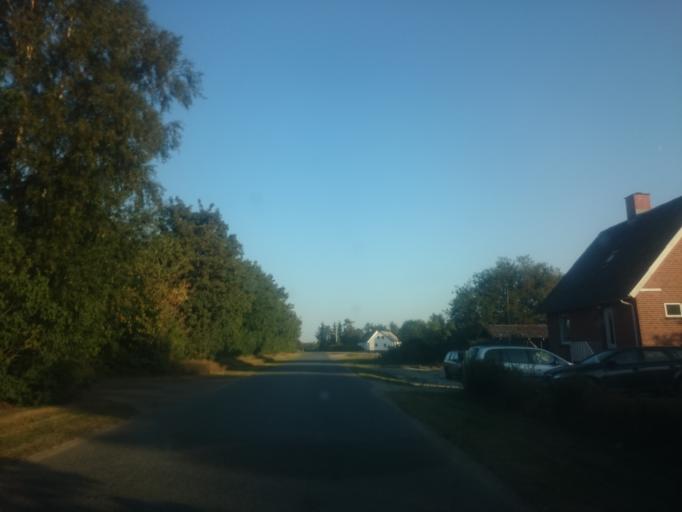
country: DK
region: South Denmark
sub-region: Billund Kommune
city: Billund
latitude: 55.7357
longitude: 9.0361
